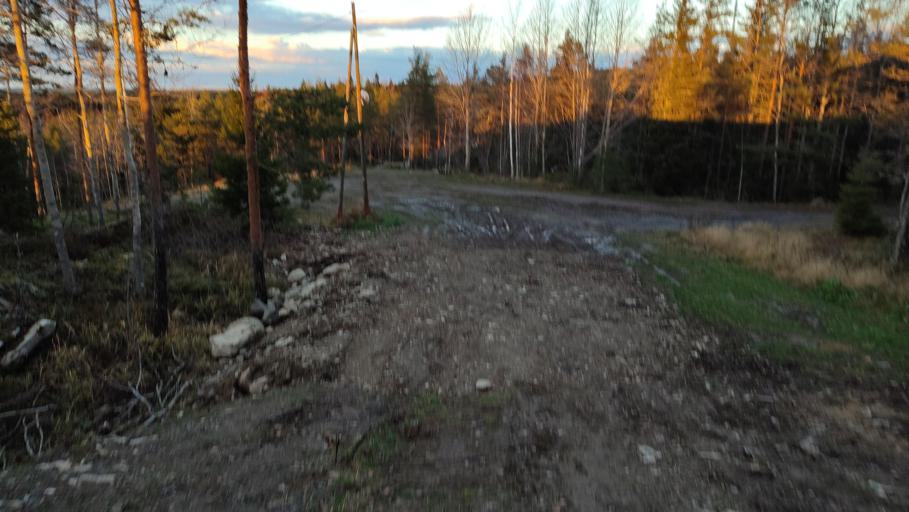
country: FI
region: Southern Ostrobothnia
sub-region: Suupohja
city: Karijoki
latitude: 62.2826
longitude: 21.6272
